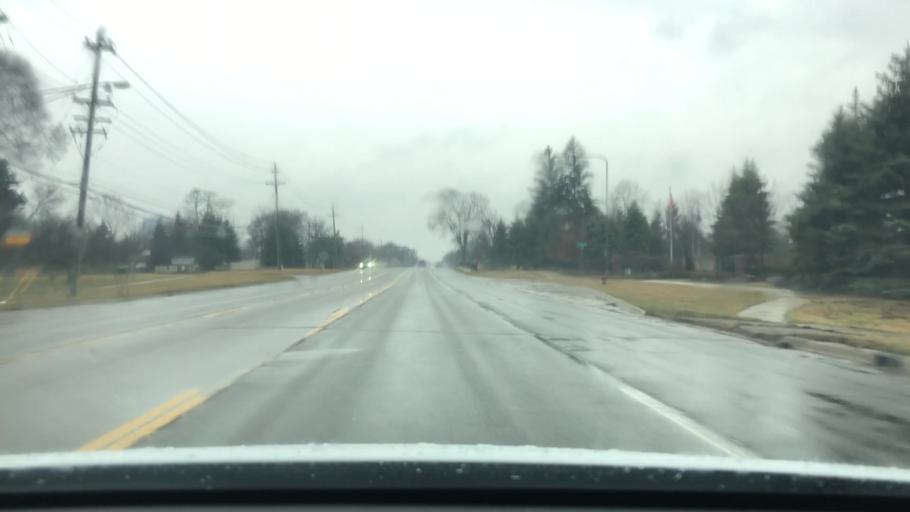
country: US
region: Michigan
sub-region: Oakland County
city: Troy
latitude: 42.5748
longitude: -83.1679
